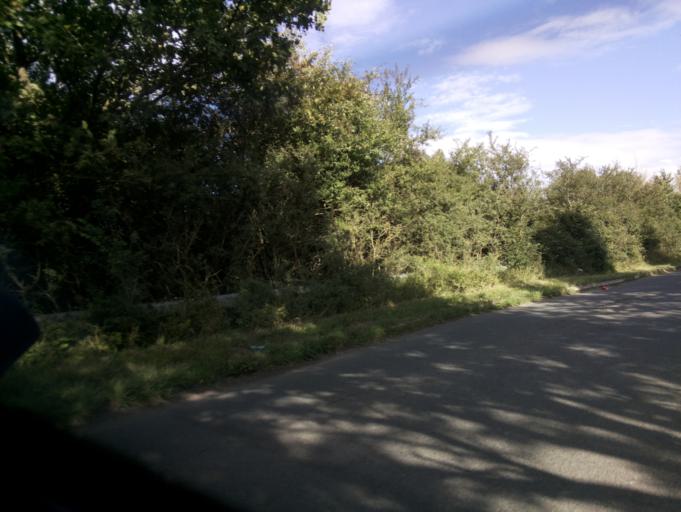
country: GB
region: England
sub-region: Gloucestershire
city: Gloucester
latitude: 51.8069
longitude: -2.2514
